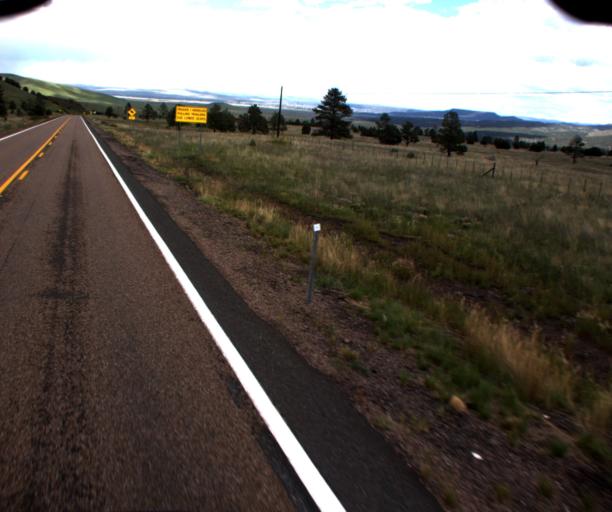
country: US
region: Arizona
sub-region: Apache County
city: Eagar
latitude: 34.0879
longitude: -109.4399
